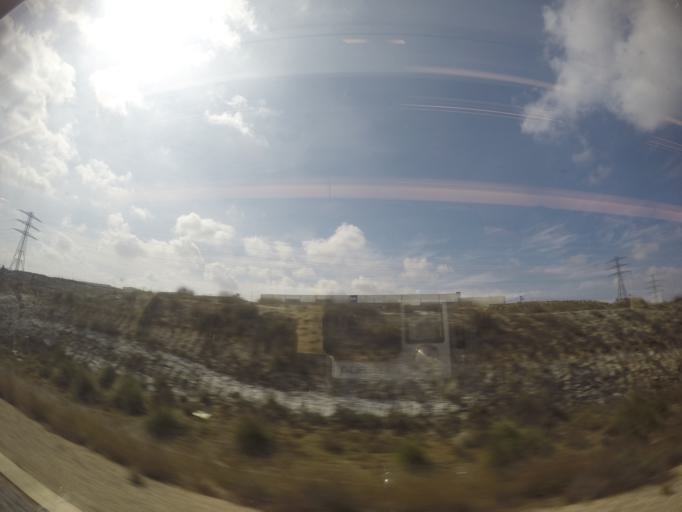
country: ES
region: Aragon
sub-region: Provincia de Zaragoza
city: El Burgo de Ebro
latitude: 41.5880
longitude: -0.8200
